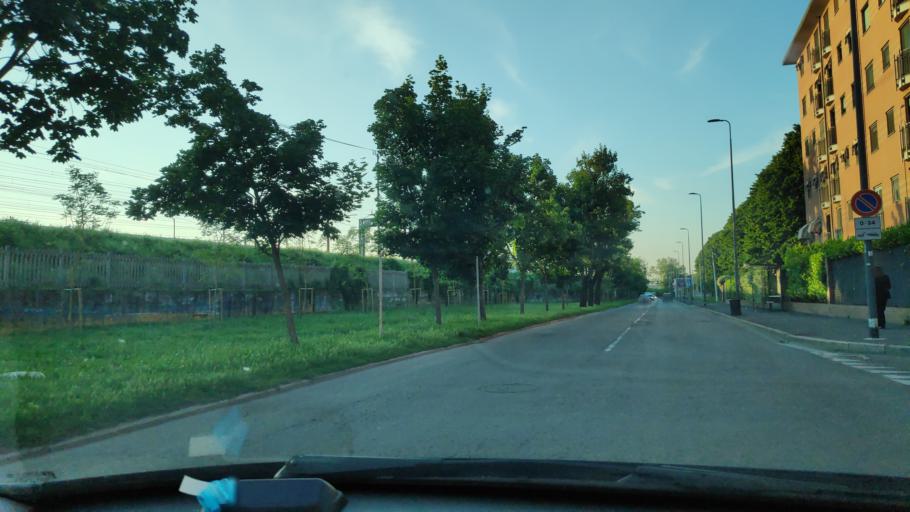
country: IT
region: Lombardy
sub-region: Citta metropolitana di Milano
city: Linate
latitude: 45.4531
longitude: 9.2378
